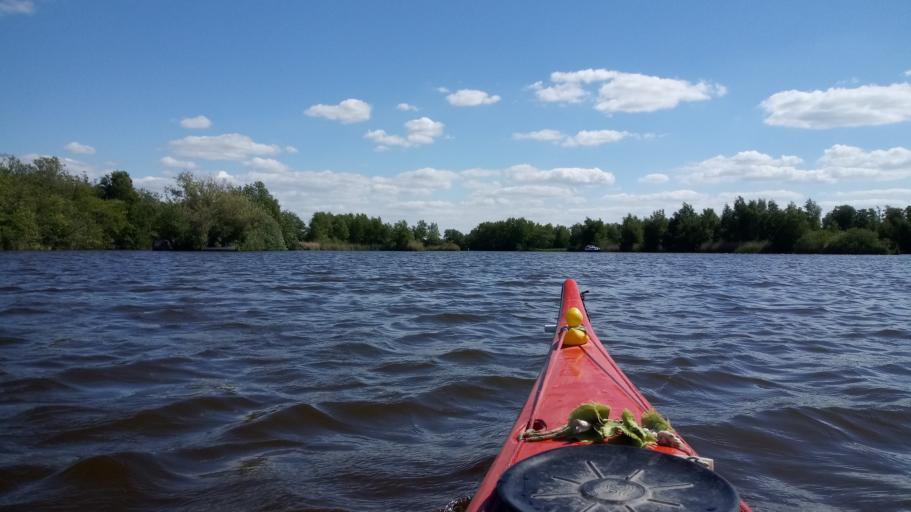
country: NL
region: South Holland
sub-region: Gemeente Nieuwkoop
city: Nieuwkoop
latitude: 52.1432
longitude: 4.7779
